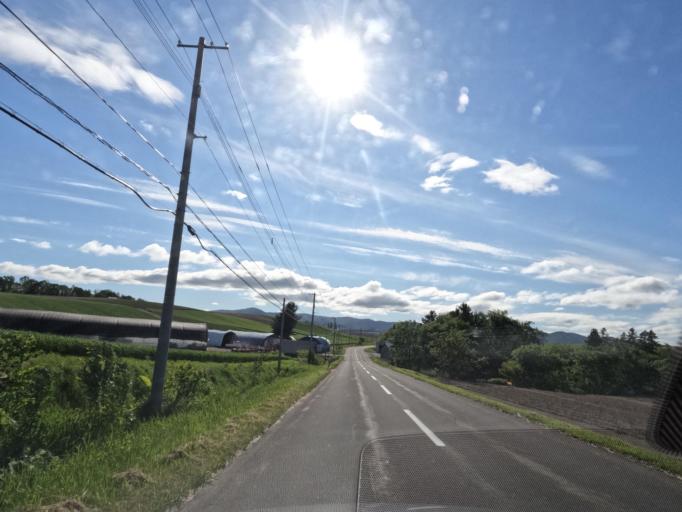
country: JP
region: Hokkaido
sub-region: Asahikawa-shi
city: Asahikawa
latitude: 43.5963
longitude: 142.4414
